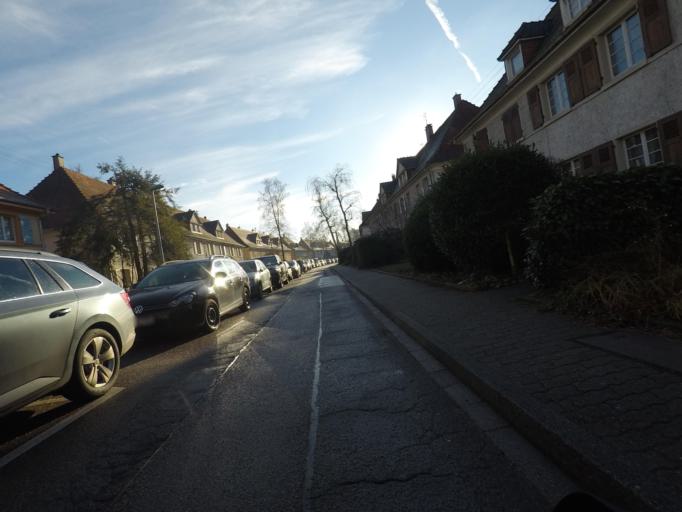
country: DE
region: Baden-Wuerttemberg
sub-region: Karlsruhe Region
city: Karlsruhe
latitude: 48.9772
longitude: 8.4100
